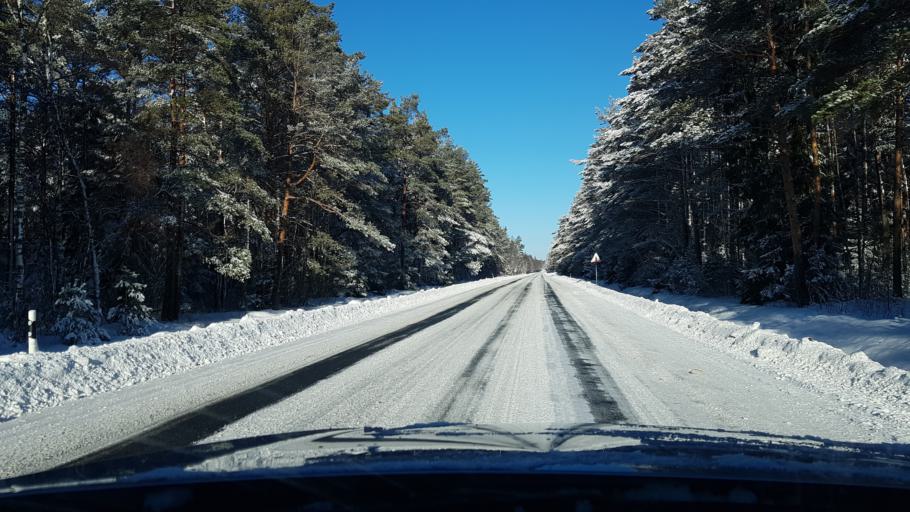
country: EE
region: Hiiumaa
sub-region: Kaerdla linn
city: Kardla
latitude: 58.9045
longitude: 22.7904
